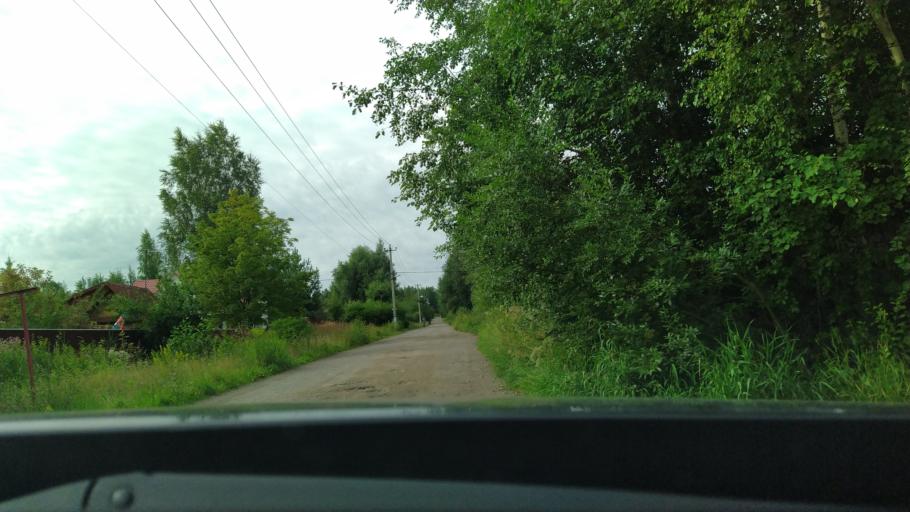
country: RU
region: Leningrad
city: Otradnoye
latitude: 59.7314
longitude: 30.8475
